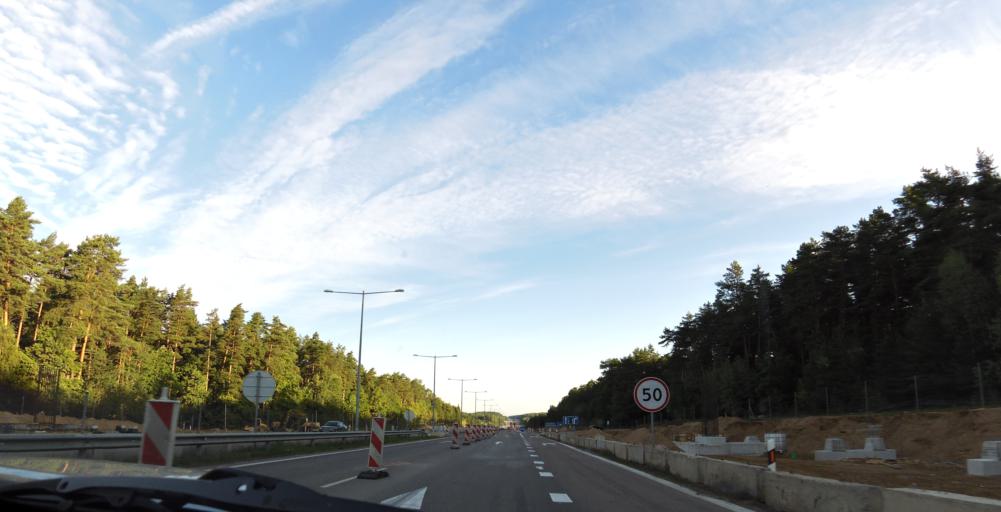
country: LT
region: Vilnius County
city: Ukmerge
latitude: 55.2468
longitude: 24.8194
